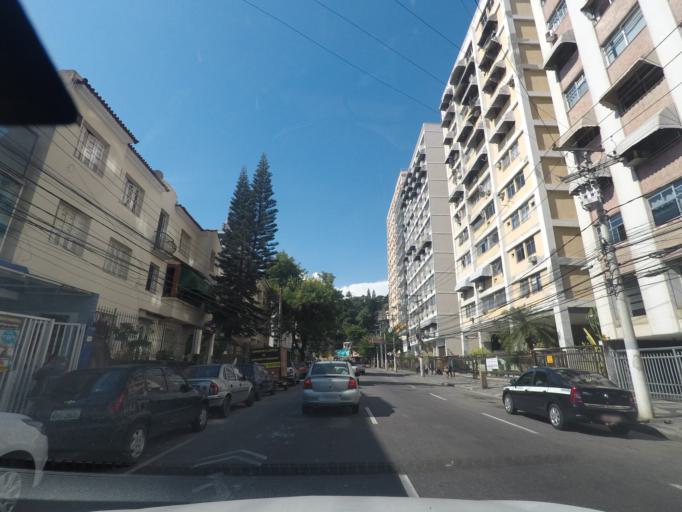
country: BR
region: Rio de Janeiro
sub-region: Niteroi
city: Niteroi
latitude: -22.9027
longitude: -43.1220
